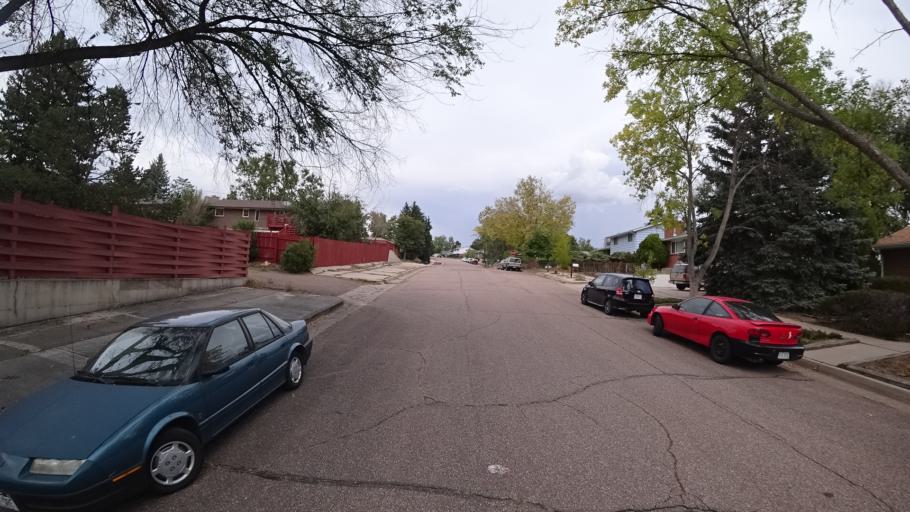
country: US
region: Colorado
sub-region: El Paso County
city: Colorado Springs
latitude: 38.8627
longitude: -104.7844
